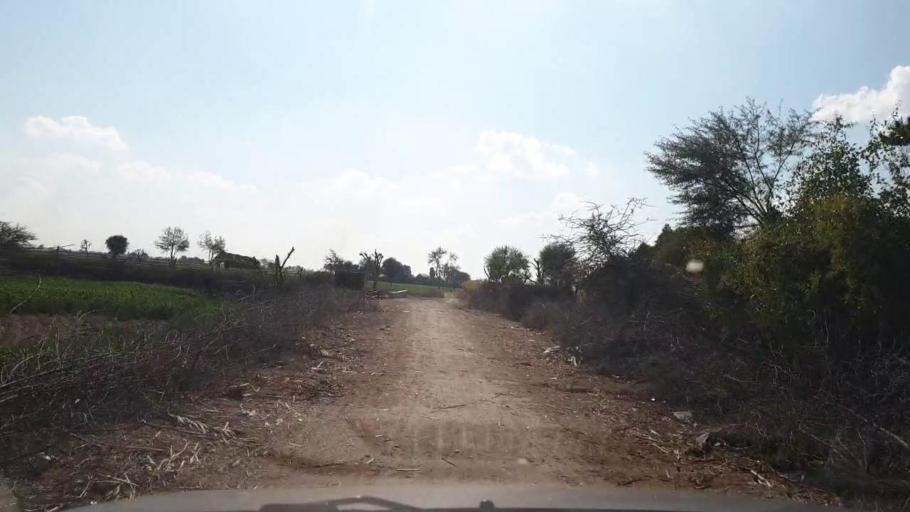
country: PK
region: Sindh
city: Sinjhoro
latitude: 26.0197
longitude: 68.7453
